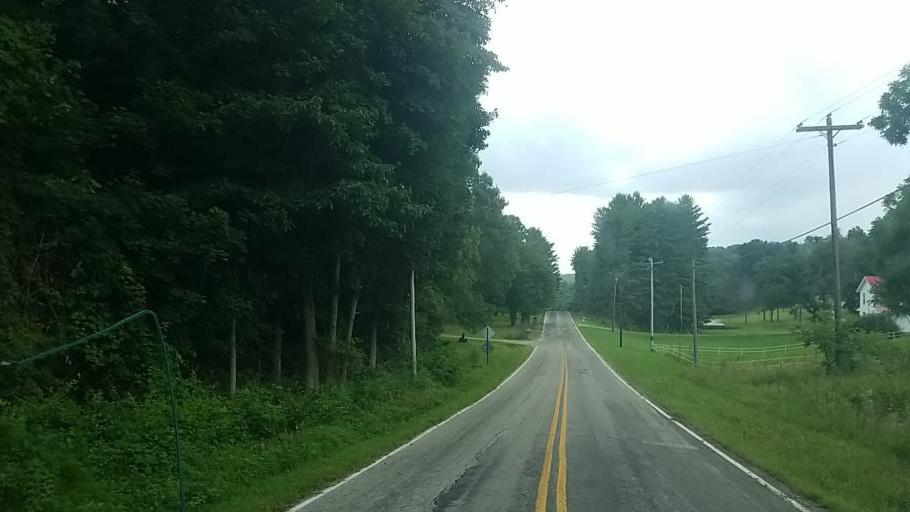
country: US
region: Ohio
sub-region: Muskingum County
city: Frazeysburg
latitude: 40.1620
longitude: -82.2570
